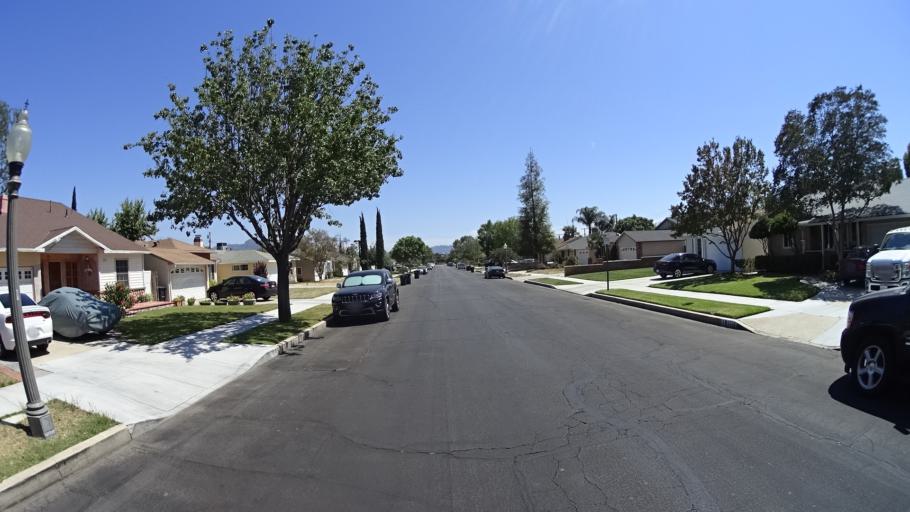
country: US
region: California
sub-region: Los Angeles County
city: North Hollywood
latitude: 34.1835
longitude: -118.3517
